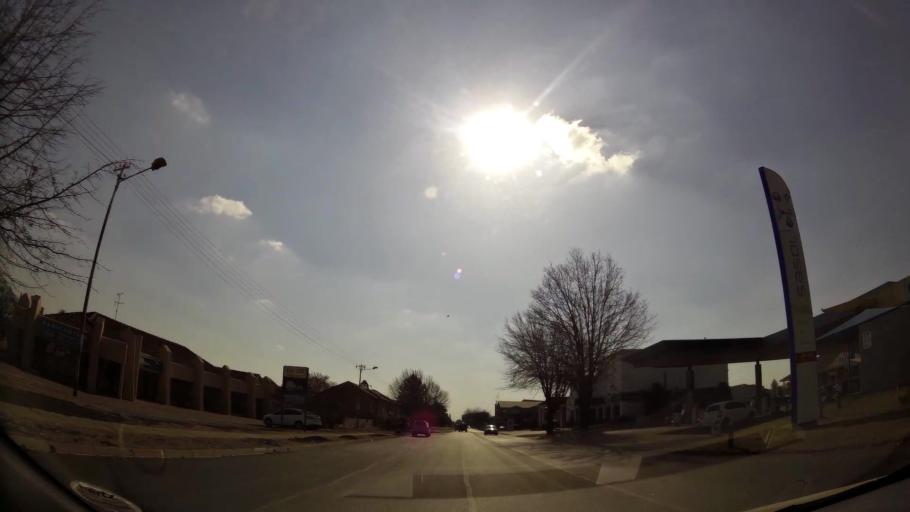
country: ZA
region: Gauteng
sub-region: West Rand District Municipality
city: Randfontein
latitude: -26.1680
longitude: 27.6983
